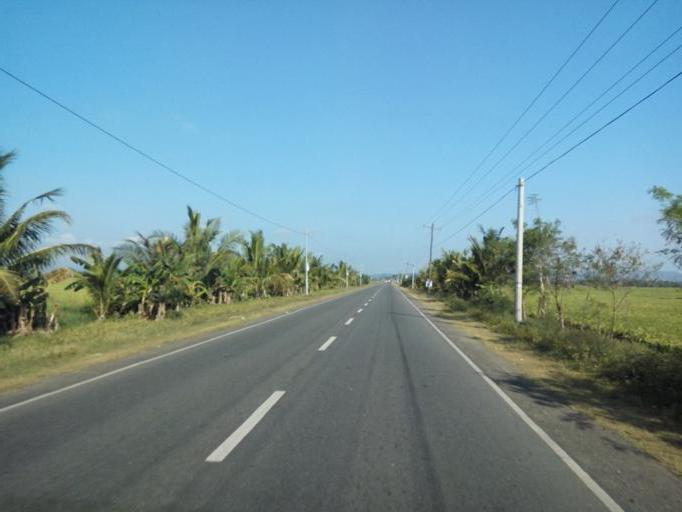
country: PH
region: Cagayan Valley
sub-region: Province of Cagayan
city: Amulung
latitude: 17.8691
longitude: 121.7104
